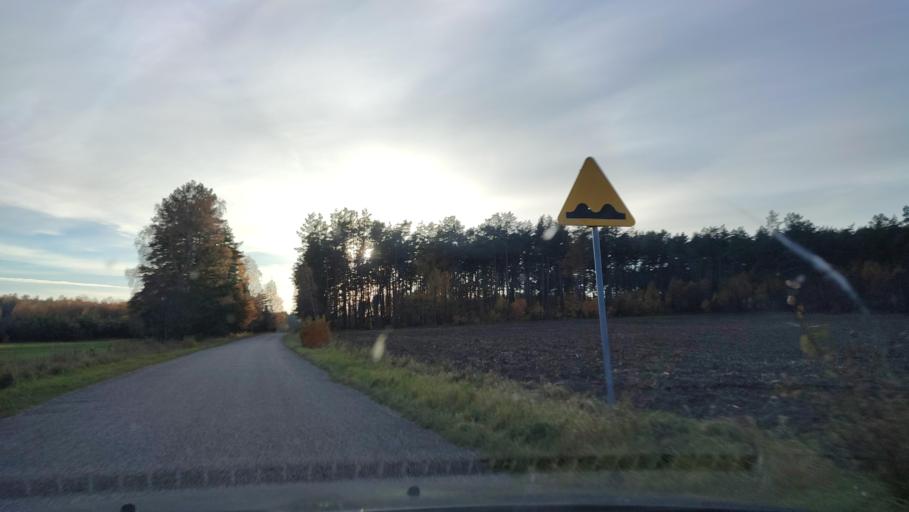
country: PL
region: Masovian Voivodeship
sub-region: Powiat przasnyski
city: Chorzele
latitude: 53.3326
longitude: 20.7413
